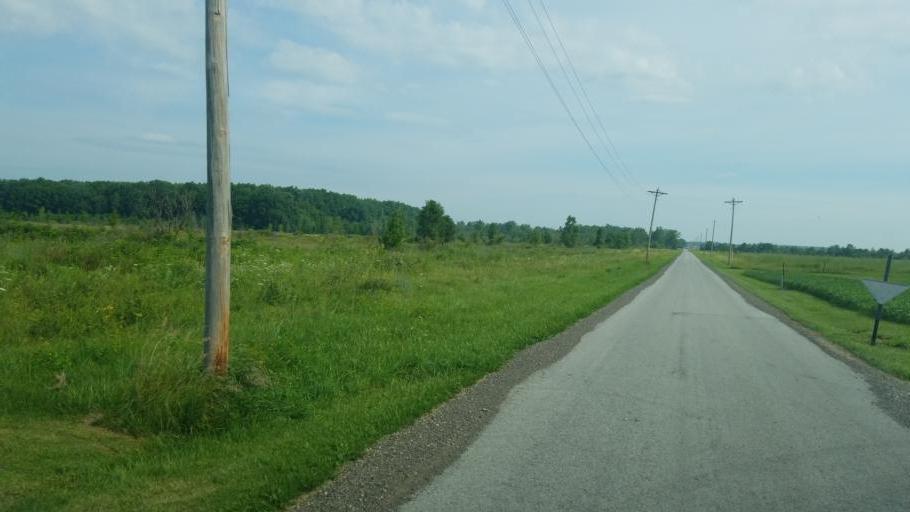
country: US
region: Ohio
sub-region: Marion County
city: Marion
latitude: 40.5680
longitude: -83.2559
